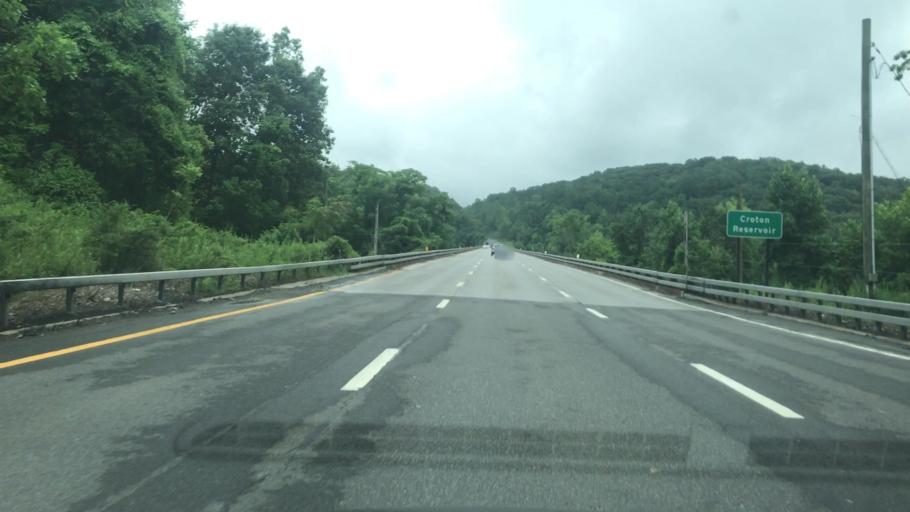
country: US
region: New York
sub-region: Westchester County
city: Yorktown Heights
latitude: 41.2415
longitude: -73.8171
